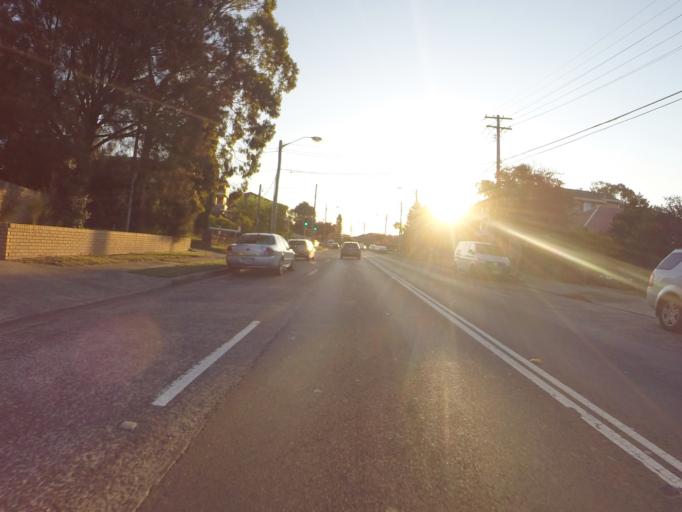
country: AU
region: New South Wales
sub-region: Rockdale
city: Bardwell Valley
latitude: -33.9254
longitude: 151.1339
